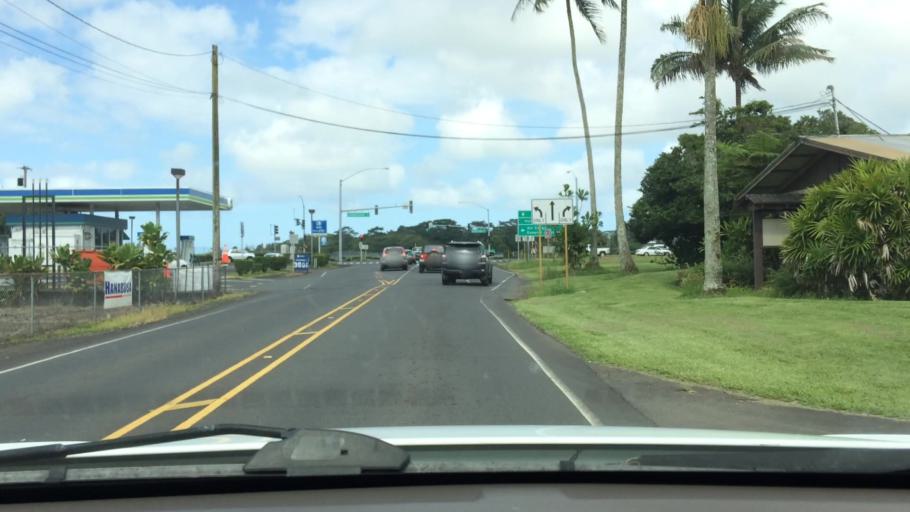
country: US
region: Hawaii
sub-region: Hawaii County
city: Hilo
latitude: 19.7117
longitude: -155.0653
